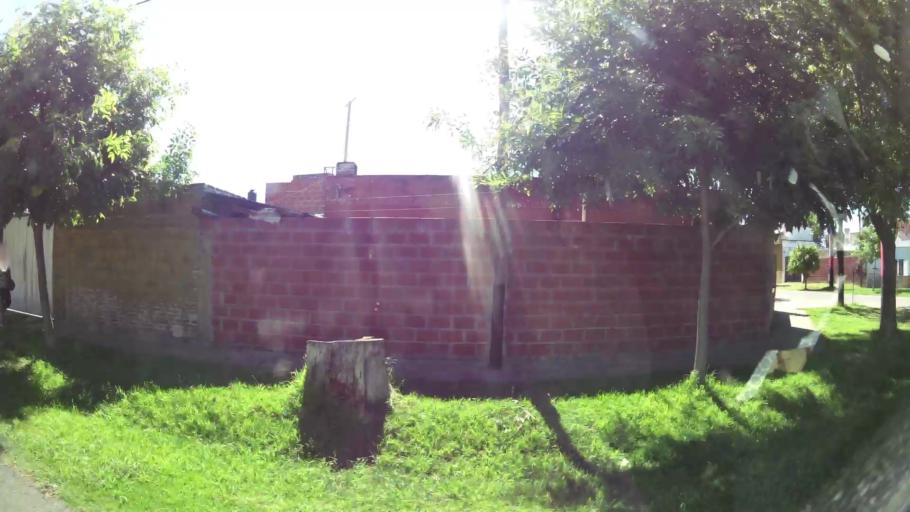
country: AR
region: Santa Fe
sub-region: Departamento de Rosario
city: Rosario
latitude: -32.9681
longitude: -60.6968
